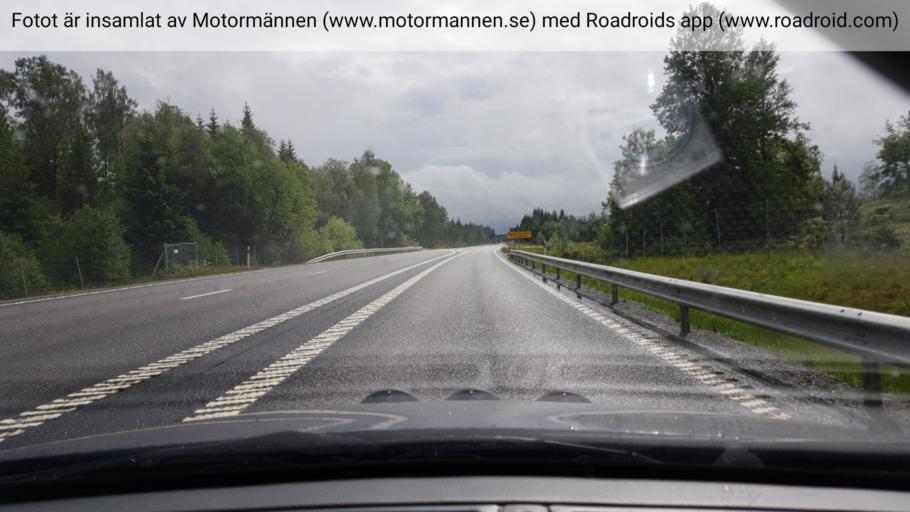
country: SE
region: Vaestra Goetaland
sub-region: Boras Kommun
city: Viskafors
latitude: 57.6332
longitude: 12.8978
